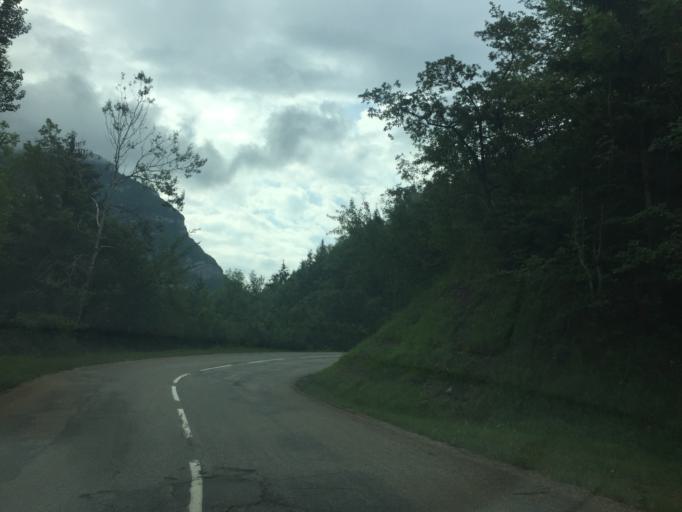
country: FR
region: Rhone-Alpes
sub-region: Departement de la Savoie
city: Challes-les-Eaux
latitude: 45.5496
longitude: 6.0316
